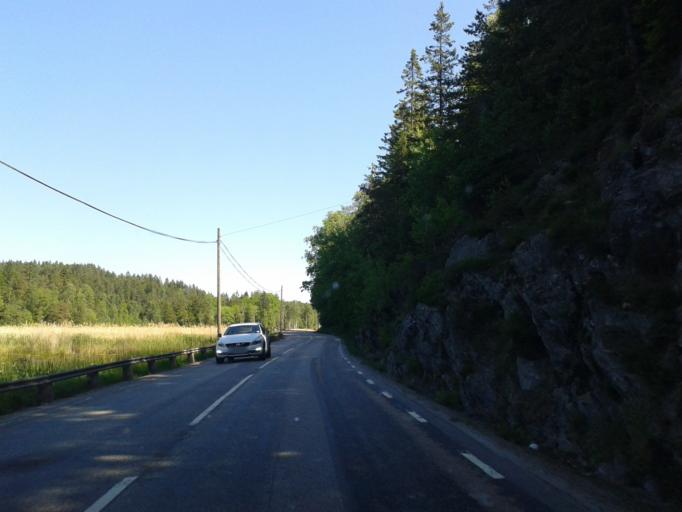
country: SE
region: Vaestra Goetaland
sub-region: Orust
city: Henan
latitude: 58.2328
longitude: 11.6937
